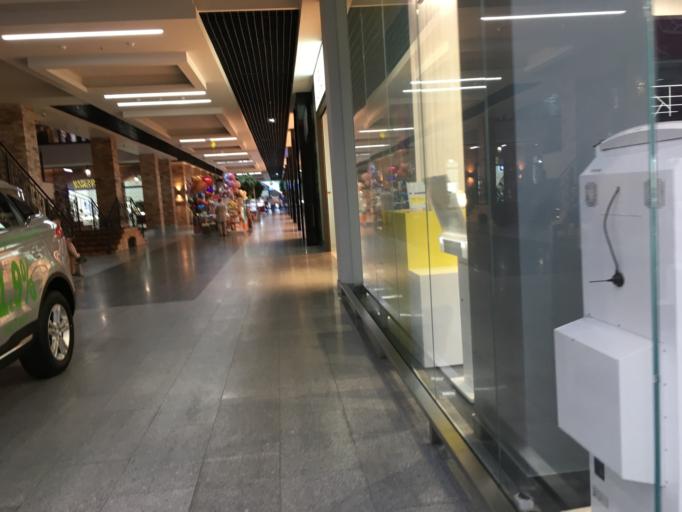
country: BY
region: Grodnenskaya
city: Hrodna
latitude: 53.7019
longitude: 23.8349
